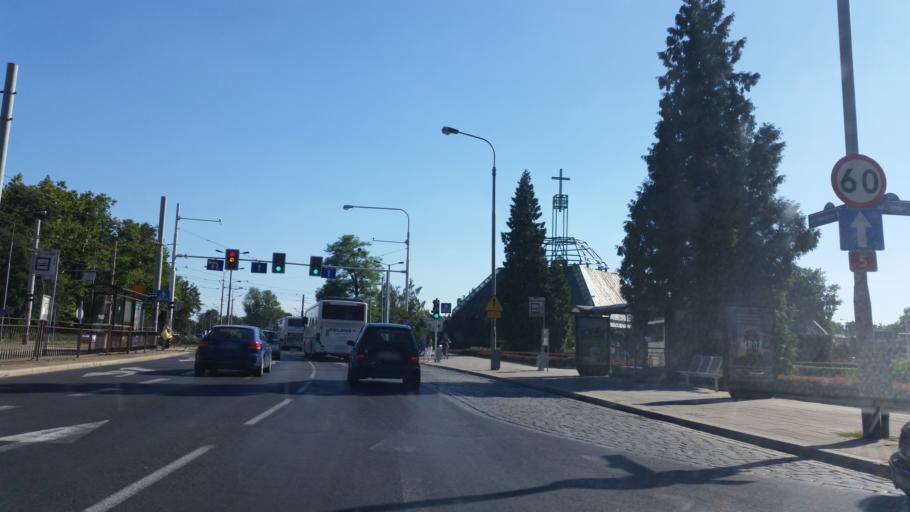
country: PL
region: Lower Silesian Voivodeship
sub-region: Powiat wroclawski
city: Wroclaw
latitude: 51.0804
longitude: 17.0080
